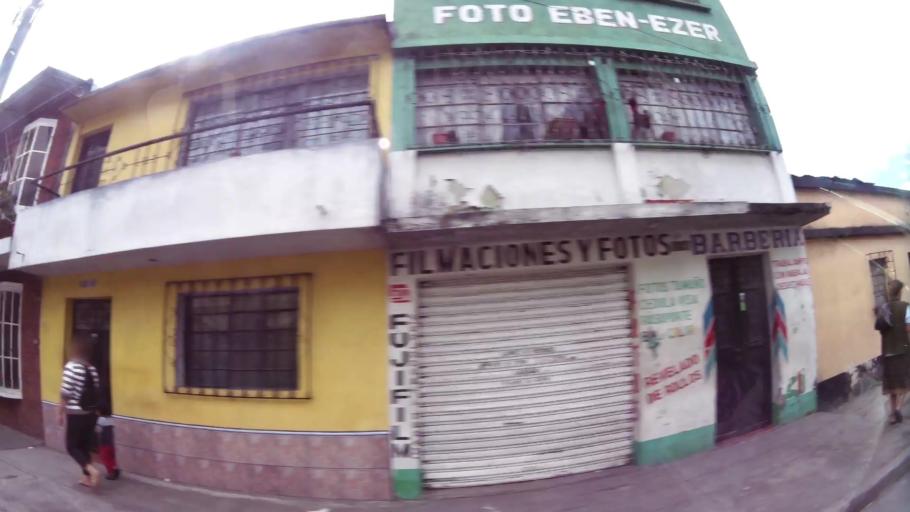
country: GT
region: Guatemala
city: Santa Catarina Pinula
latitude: 14.5672
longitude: -90.5351
